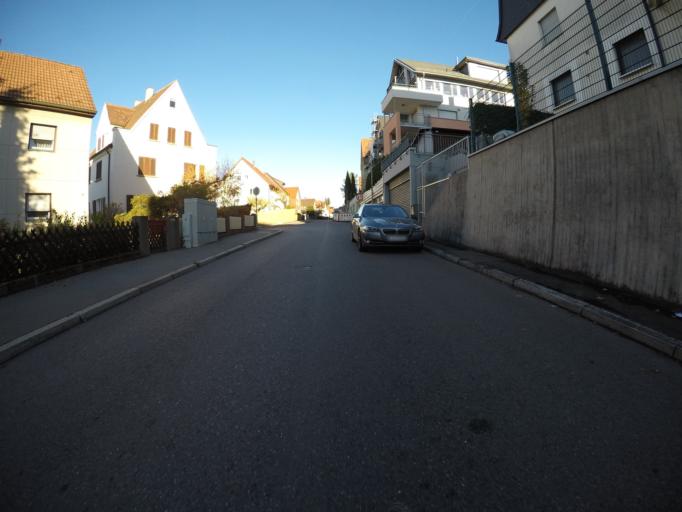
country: DE
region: Baden-Wuerttemberg
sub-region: Regierungsbezirk Stuttgart
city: Boeblingen
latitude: 48.6909
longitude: 9.0118
